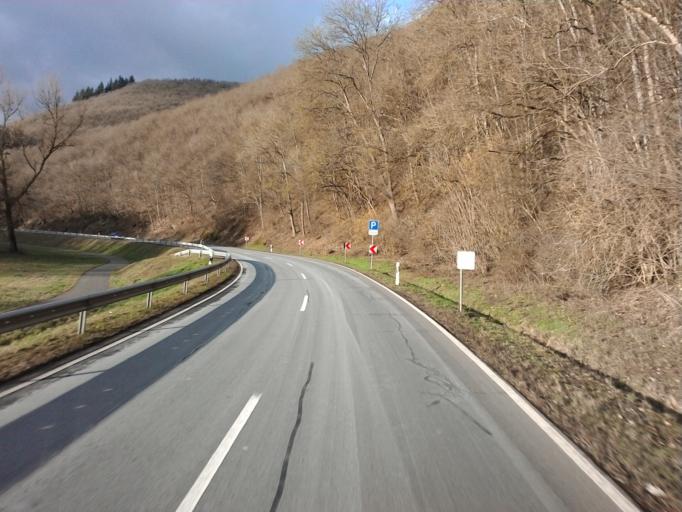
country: DE
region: Rheinland-Pfalz
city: Niederraden
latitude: 49.9870
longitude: 6.3145
